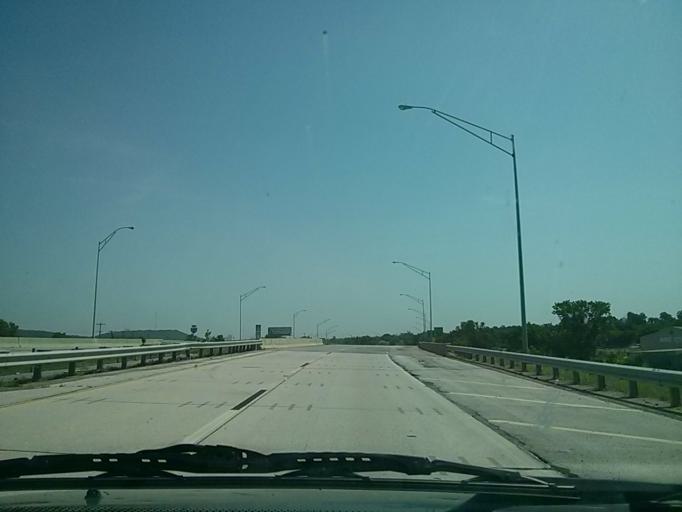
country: US
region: Oklahoma
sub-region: Tulsa County
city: Oakhurst
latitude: 36.0934
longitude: -96.0352
